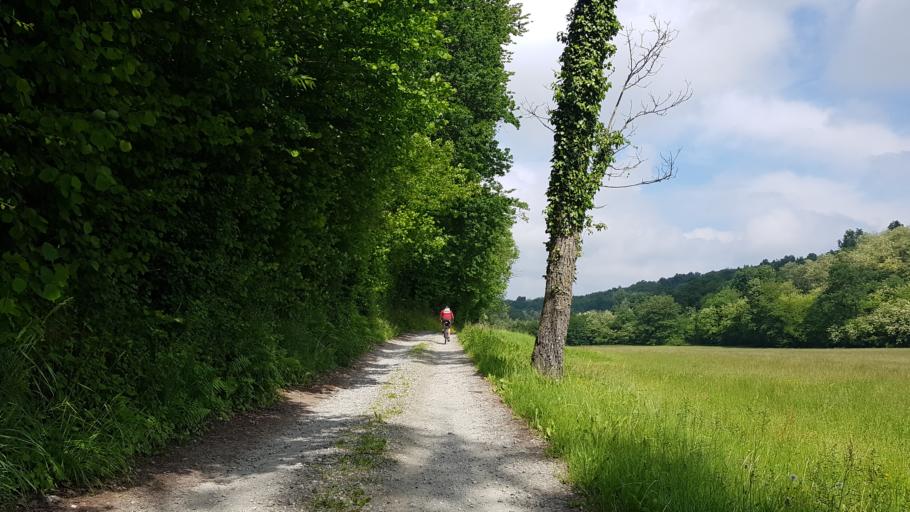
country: IT
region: Piedmont
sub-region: Provincia di Torino
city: Vialfre
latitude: 45.3805
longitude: 7.8109
